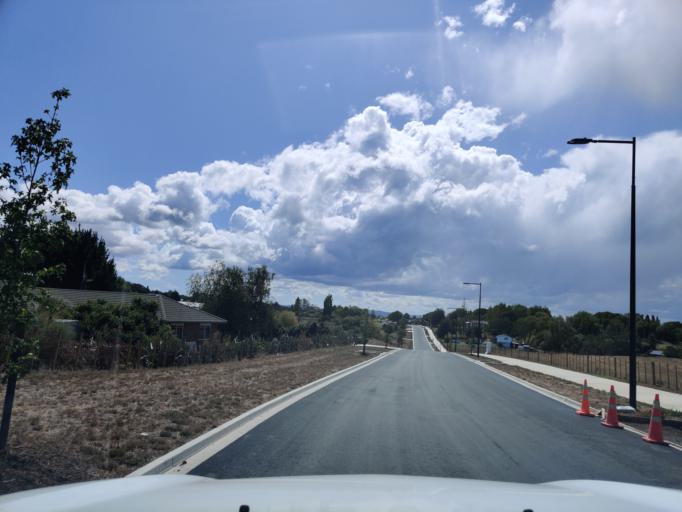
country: NZ
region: Waikato
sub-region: Waikato District
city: Te Kauwhata
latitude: -37.4114
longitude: 175.1457
